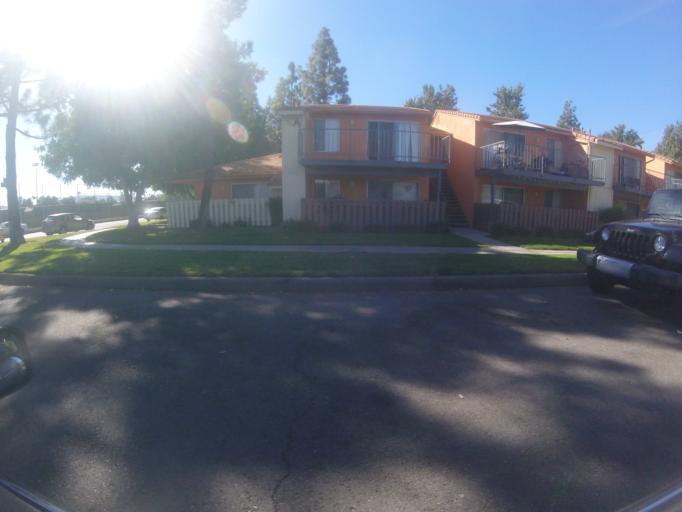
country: US
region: California
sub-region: San Bernardino County
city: Redlands
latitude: 34.0685
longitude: -117.1608
